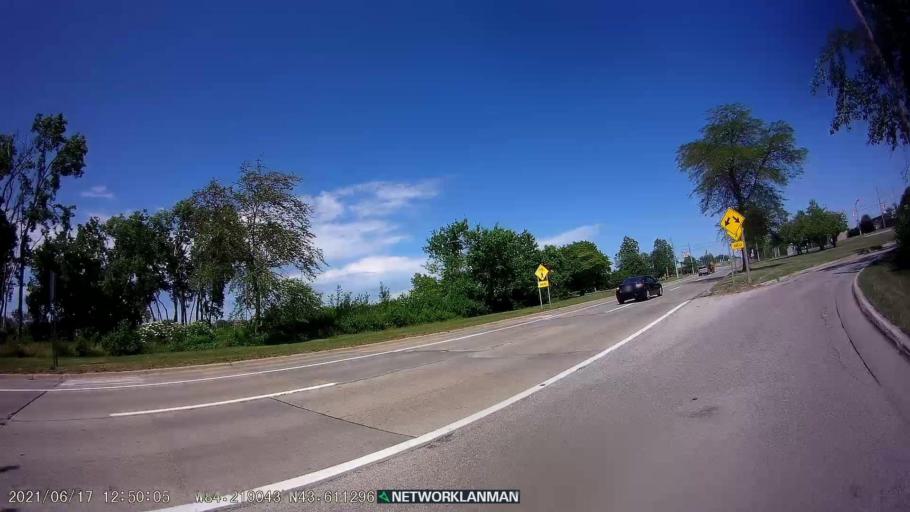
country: US
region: Michigan
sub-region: Midland County
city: Midland
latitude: 43.6110
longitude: -84.2178
